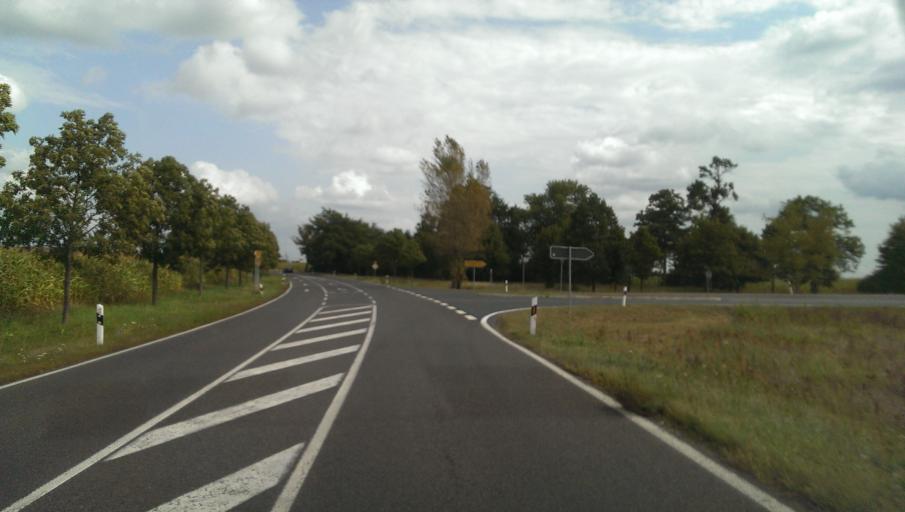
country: DE
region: Brandenburg
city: Trebbin
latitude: 52.2161
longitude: 13.2988
